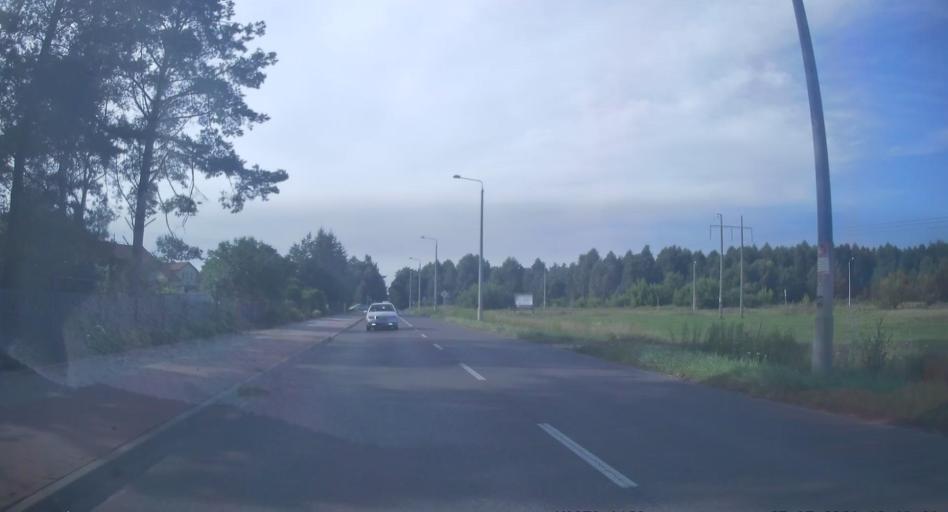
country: PL
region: Swietokrzyskie
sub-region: Powiat konecki
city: Konskie
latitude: 51.2166
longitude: 20.3912
